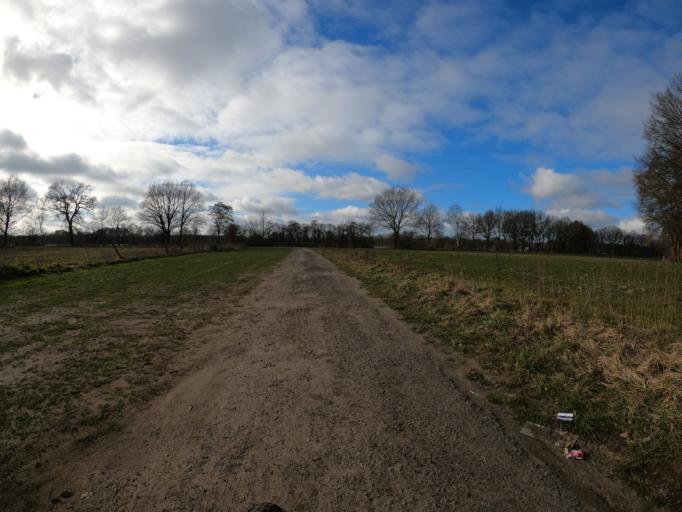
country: DE
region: Lower Saxony
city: Haselunne
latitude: 52.6741
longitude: 7.5223
